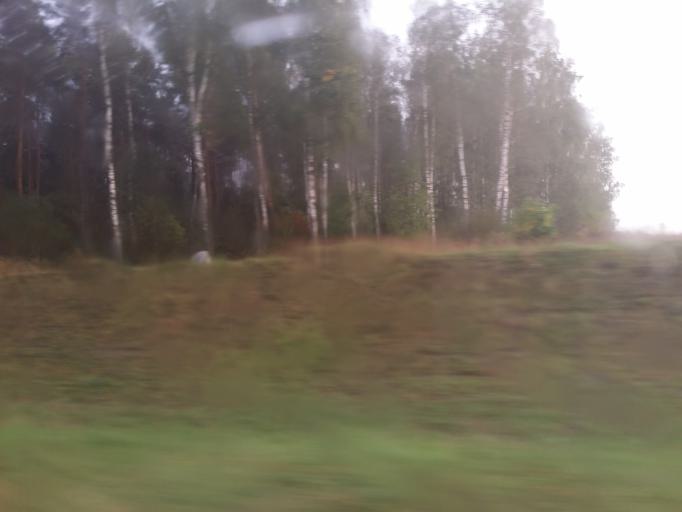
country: BY
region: Minsk
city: Smilavichy
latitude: 53.7655
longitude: 28.1874
